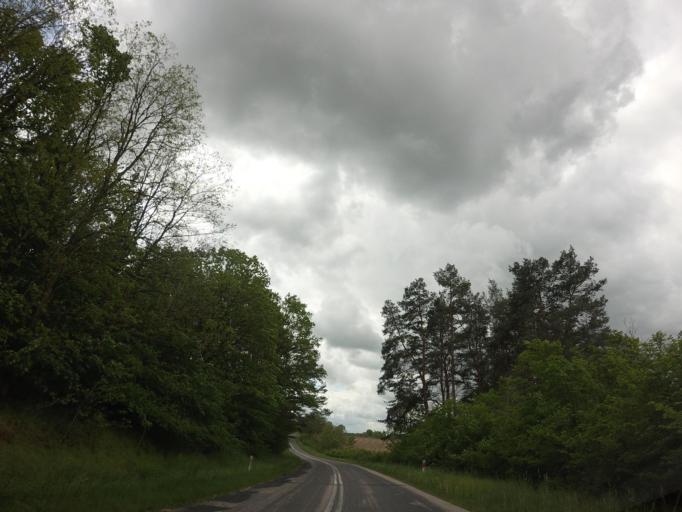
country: PL
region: West Pomeranian Voivodeship
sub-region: Powiat stargardzki
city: Suchan
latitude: 53.2199
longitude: 15.2924
